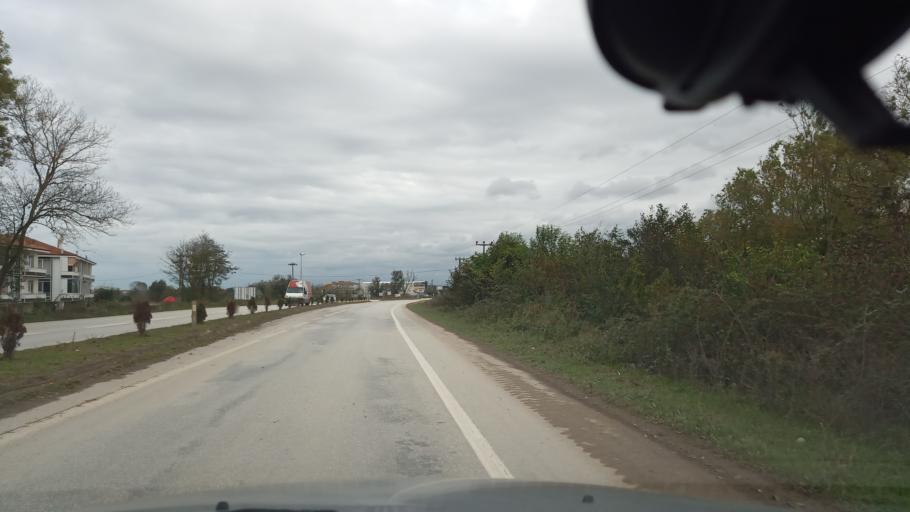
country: TR
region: Sakarya
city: Karasu
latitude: 41.1178
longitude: 30.6493
